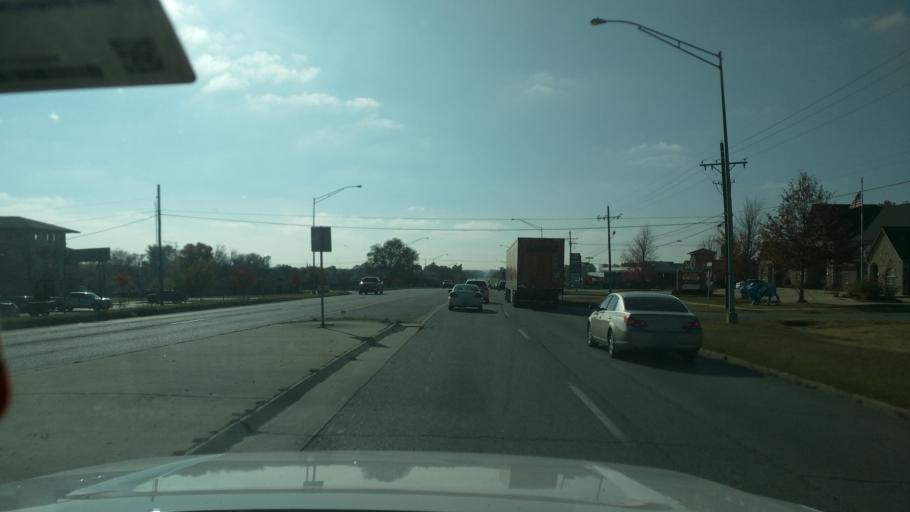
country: US
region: Oklahoma
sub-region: Washington County
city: Bartlesville
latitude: 36.7266
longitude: -95.9352
